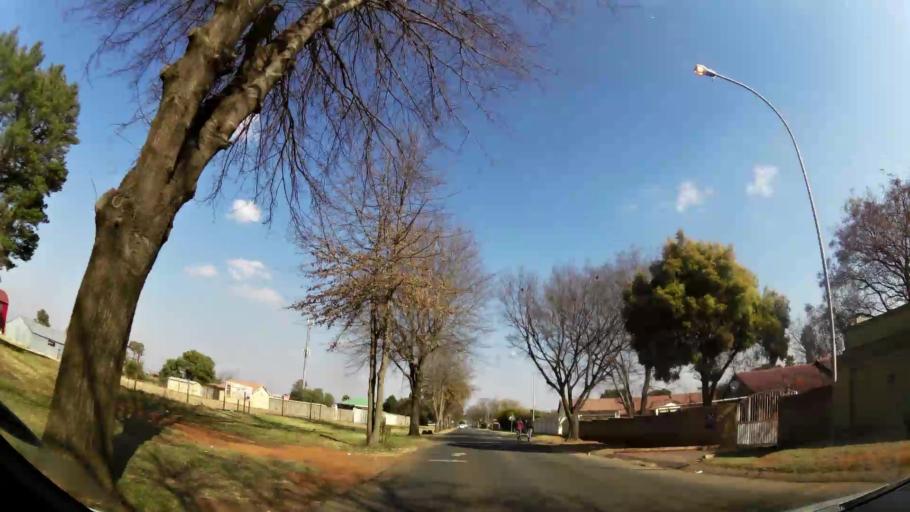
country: ZA
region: Gauteng
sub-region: Ekurhuleni Metropolitan Municipality
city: Brakpan
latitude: -26.2452
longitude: 28.3161
